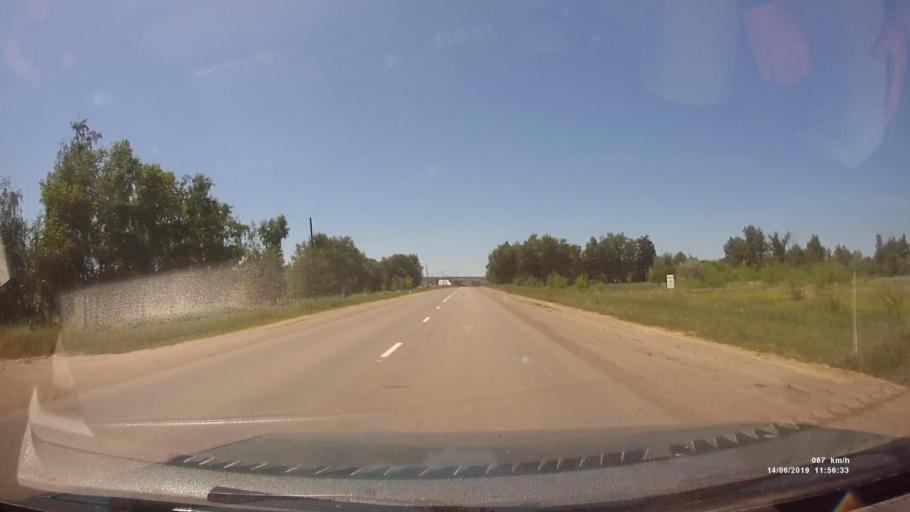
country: RU
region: Rostov
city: Kazanskaya
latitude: 49.8023
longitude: 41.1601
